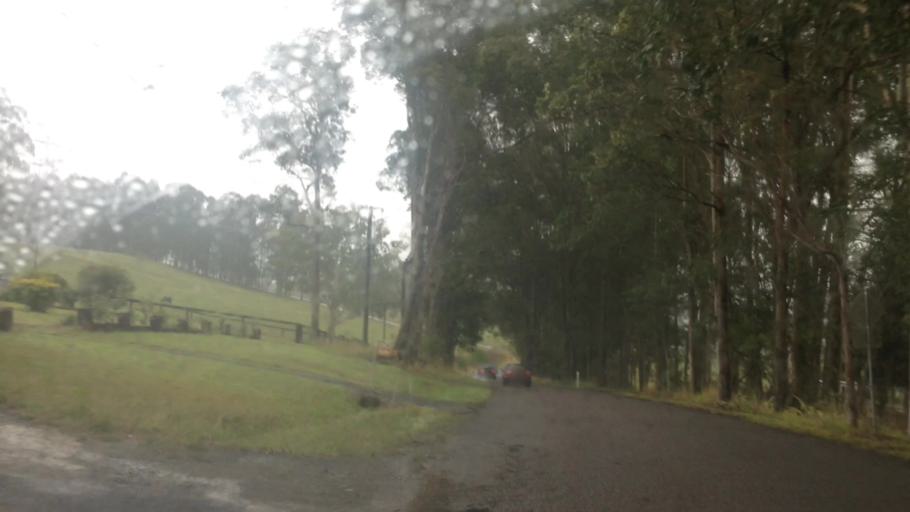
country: AU
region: New South Wales
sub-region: Wyong Shire
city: Little Jilliby
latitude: -33.2006
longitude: 151.3631
